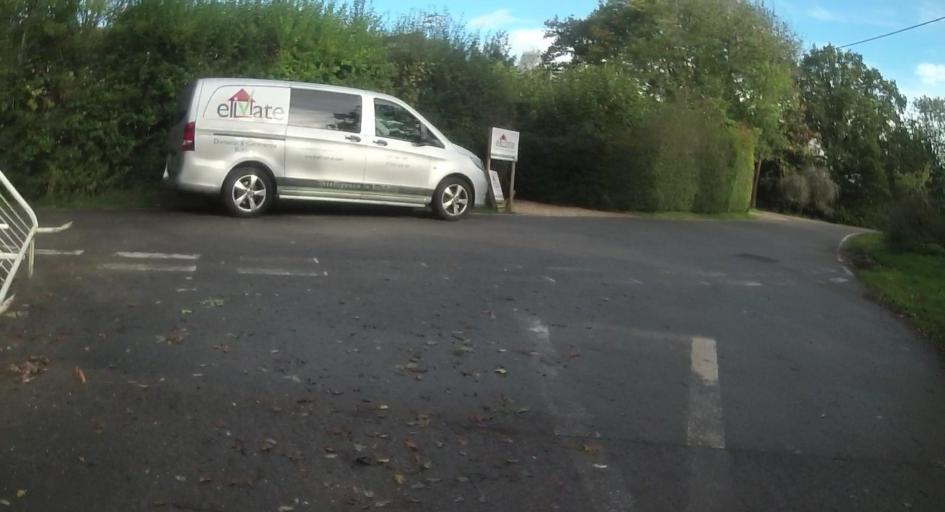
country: GB
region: England
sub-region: Wokingham
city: Shinfield
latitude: 51.3962
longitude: -0.9587
